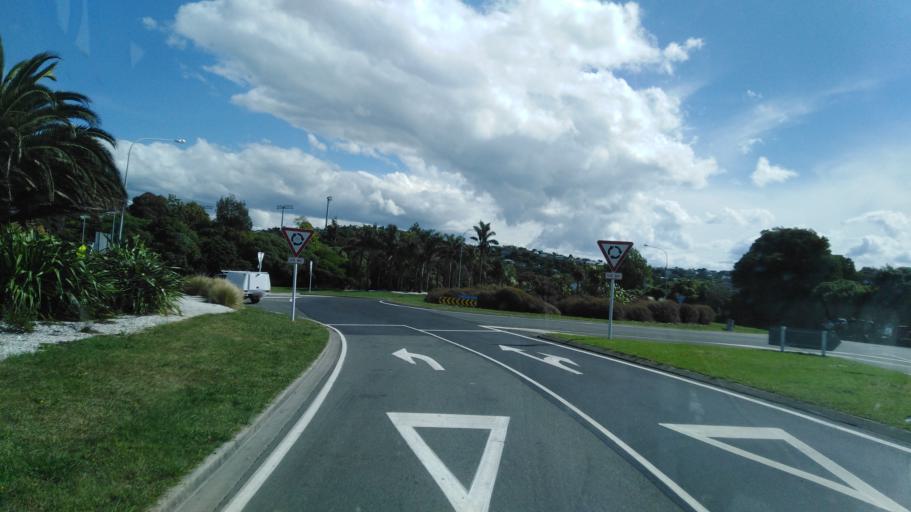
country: NZ
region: Nelson
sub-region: Nelson City
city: Nelson
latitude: -41.2649
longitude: 173.2846
